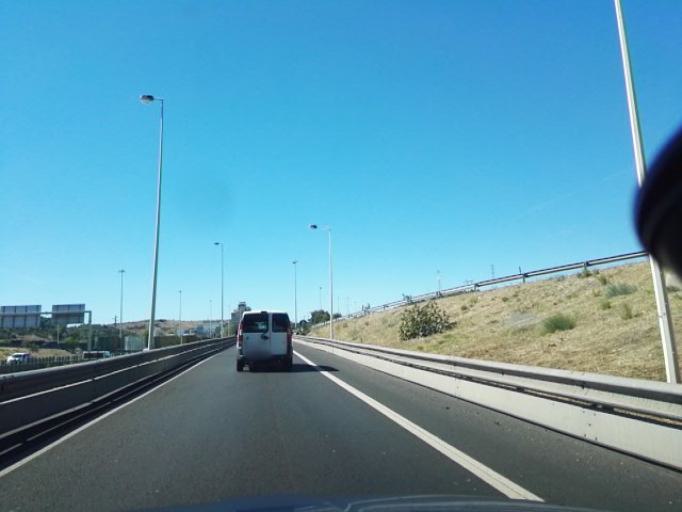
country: PT
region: Lisbon
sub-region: Vila Franca de Xira
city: Vialonga
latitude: 38.8915
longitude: -9.0508
